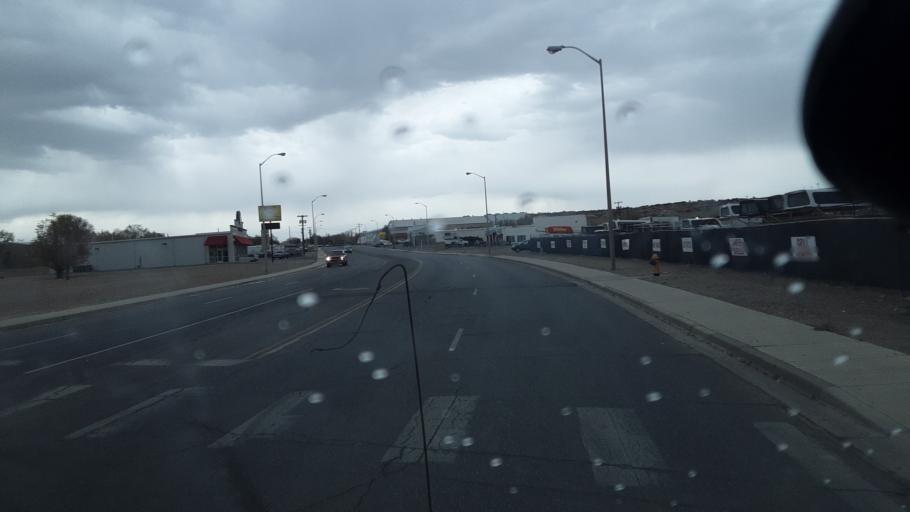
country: US
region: New Mexico
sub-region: San Juan County
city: Farmington
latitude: 36.7372
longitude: -108.1774
